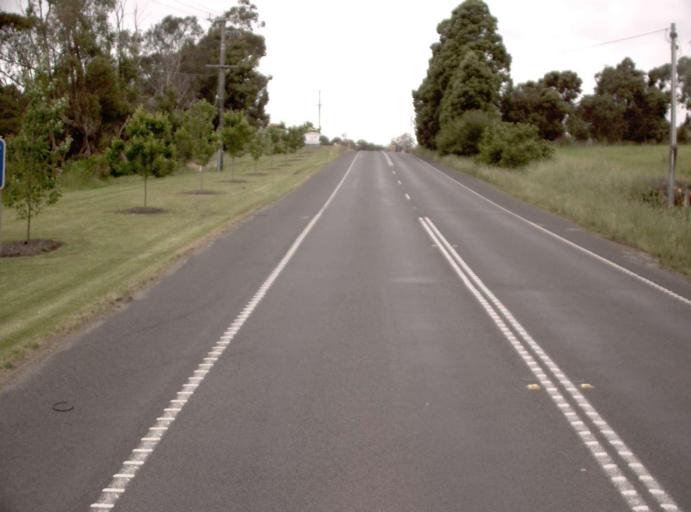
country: AU
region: Victoria
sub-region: Baw Baw
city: Warragul
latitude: -38.4694
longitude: 145.9393
